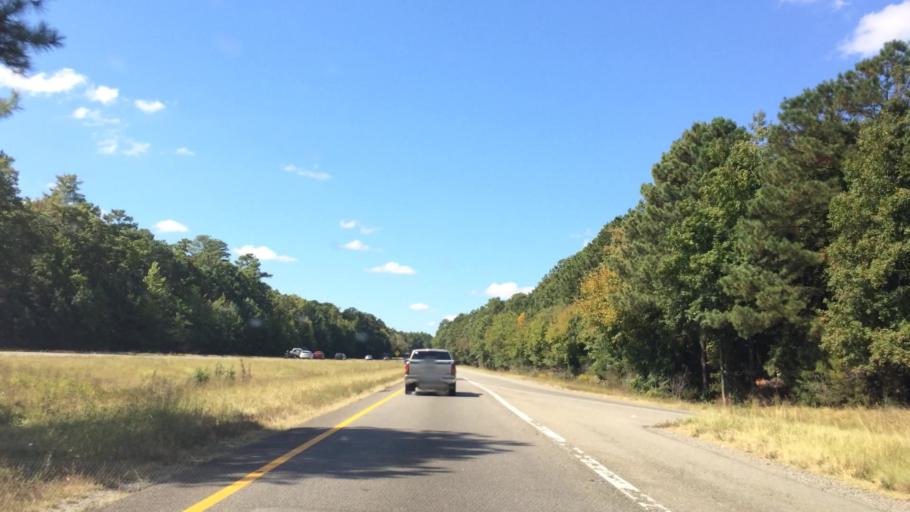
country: US
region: Virginia
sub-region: Henrico County
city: Glen Allen
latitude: 37.6597
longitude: -77.4631
